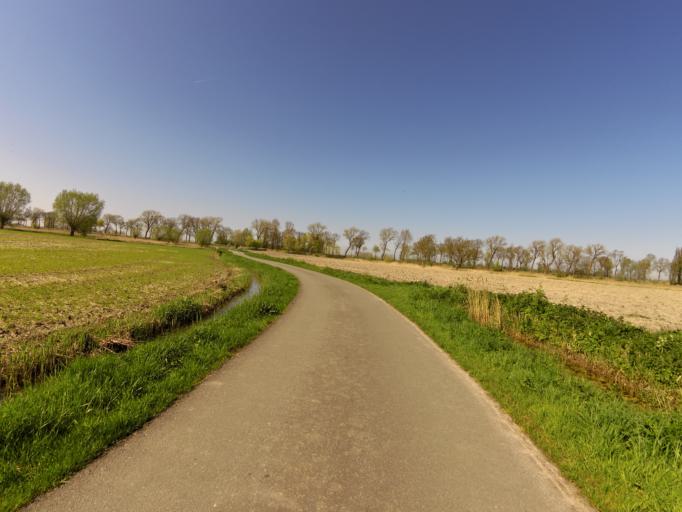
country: BE
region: Flanders
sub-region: Provincie West-Vlaanderen
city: Jabbeke
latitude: 51.1990
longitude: 3.0672
